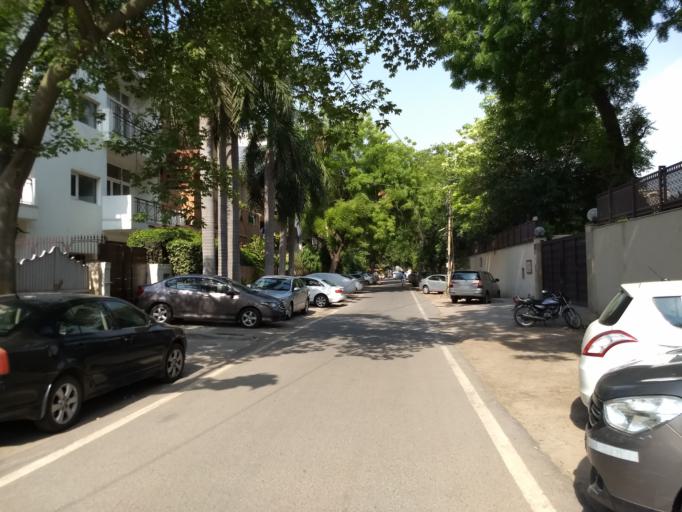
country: IN
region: NCT
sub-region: New Delhi
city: New Delhi
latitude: 28.5666
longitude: 77.1975
